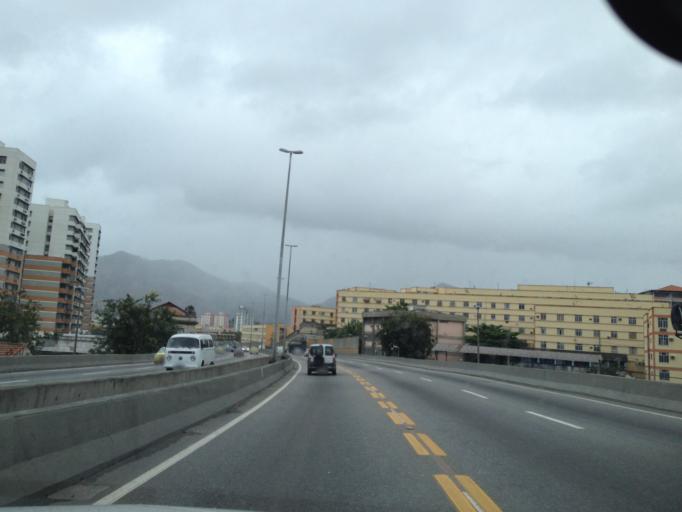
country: BR
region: Rio de Janeiro
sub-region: Rio De Janeiro
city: Rio de Janeiro
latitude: -22.8839
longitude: -43.2901
